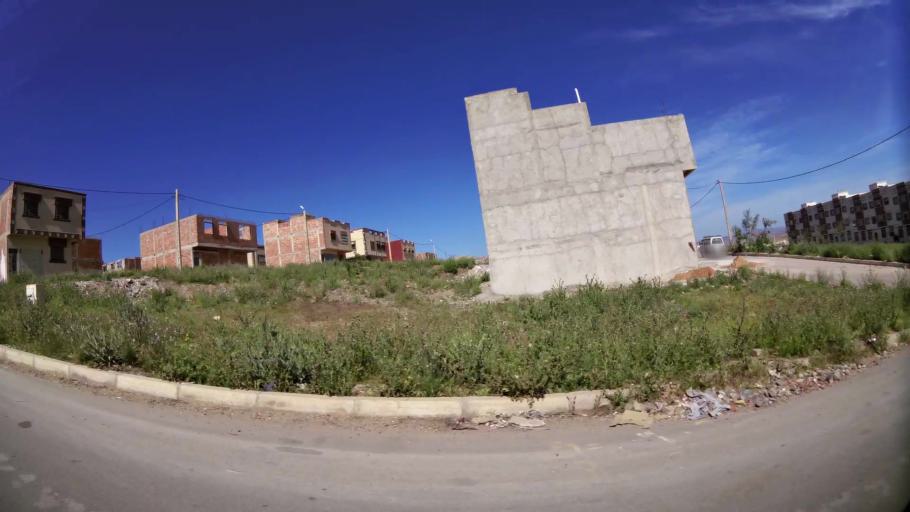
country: MA
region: Oriental
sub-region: Oujda-Angad
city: Oujda
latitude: 34.6539
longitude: -1.9417
